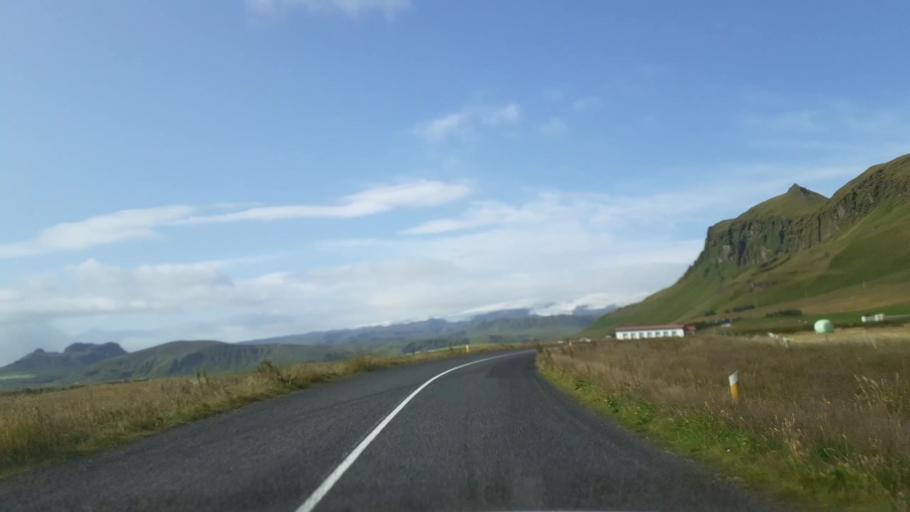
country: IS
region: South
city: Vestmannaeyjar
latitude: 63.4176
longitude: -19.0485
